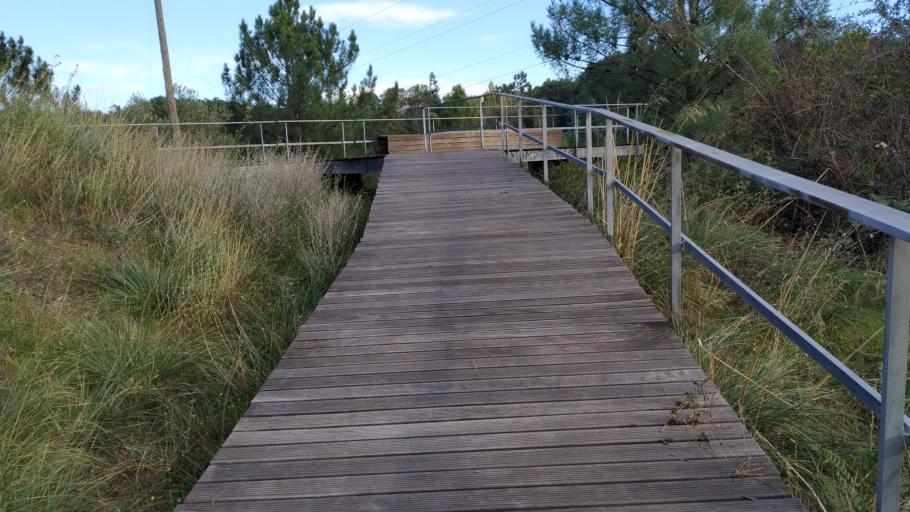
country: PT
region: Vila Real
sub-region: Vila Real
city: Vila Real
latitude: 41.2910
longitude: -7.7466
